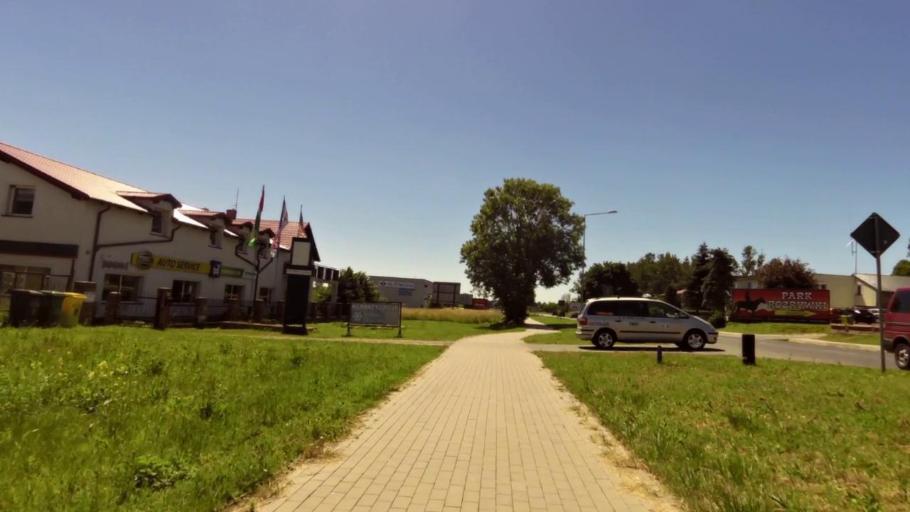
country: PL
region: West Pomeranian Voivodeship
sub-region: Powiat kolobrzeski
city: Kolobrzeg
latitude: 54.1388
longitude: 15.5592
